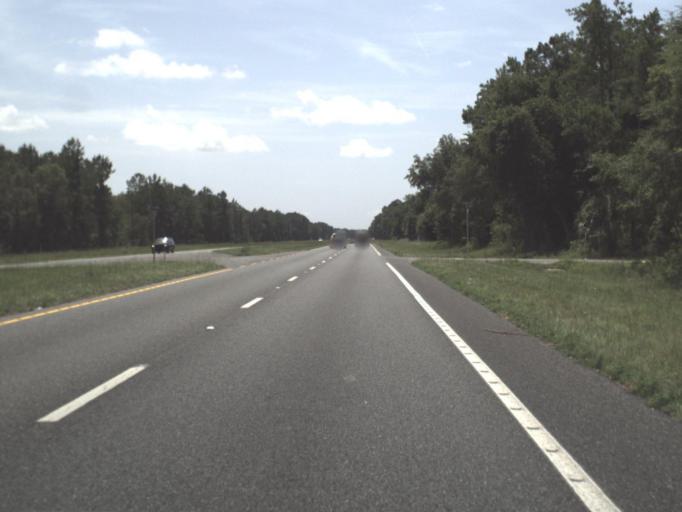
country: US
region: Florida
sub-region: Taylor County
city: Perry
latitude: 30.0059
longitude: -83.5138
